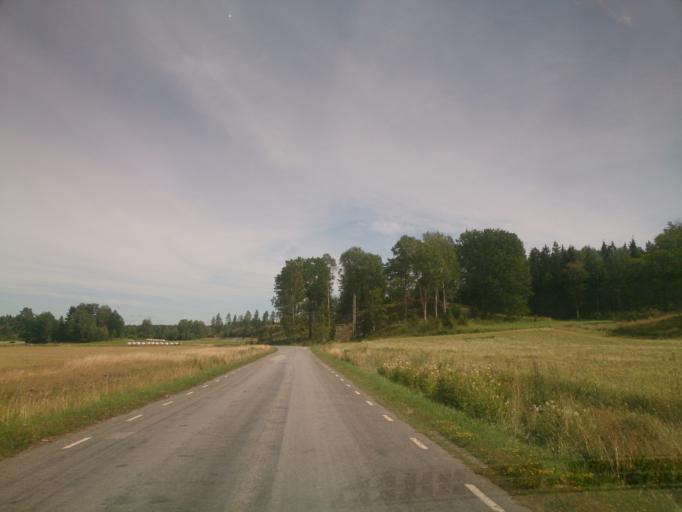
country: SE
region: OEstergoetland
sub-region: Valdemarsviks Kommun
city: Gusum
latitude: 58.3140
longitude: 16.5621
